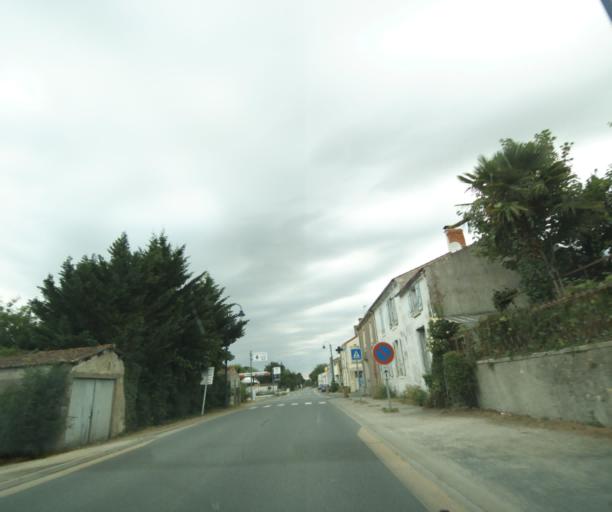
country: FR
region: Pays de la Loire
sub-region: Departement de la Vendee
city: Chaille-les-Marais
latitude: 46.3942
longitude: -1.0242
